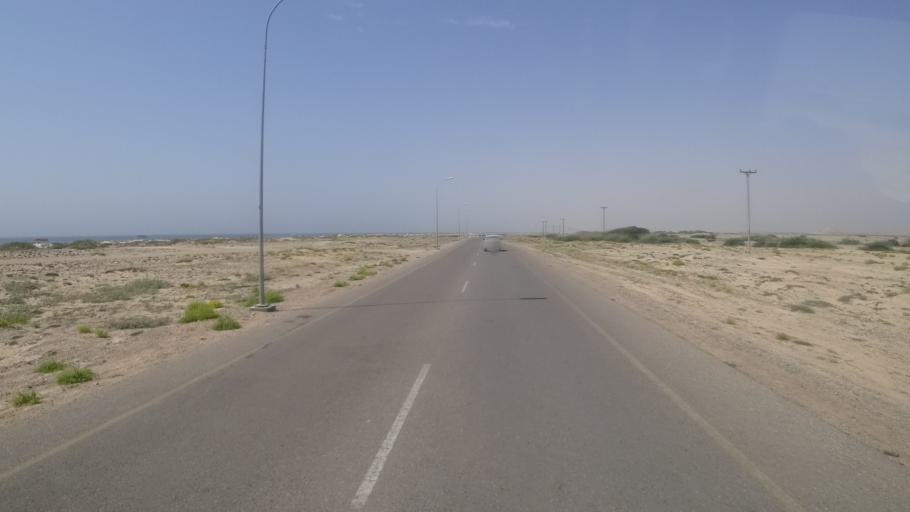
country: OM
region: Ash Sharqiyah
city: Sur
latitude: 22.1063
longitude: 59.7069
